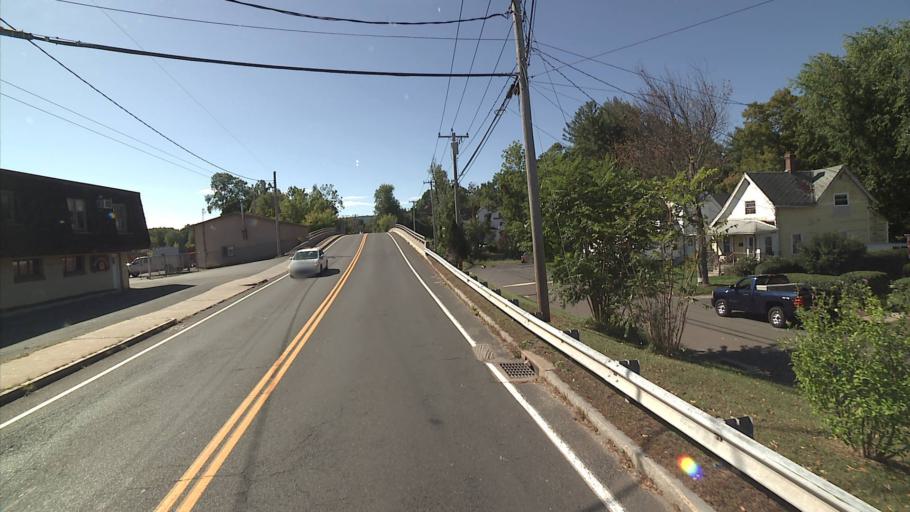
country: US
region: Connecticut
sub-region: Hartford County
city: Bristol
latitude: 41.6864
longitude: -72.9425
